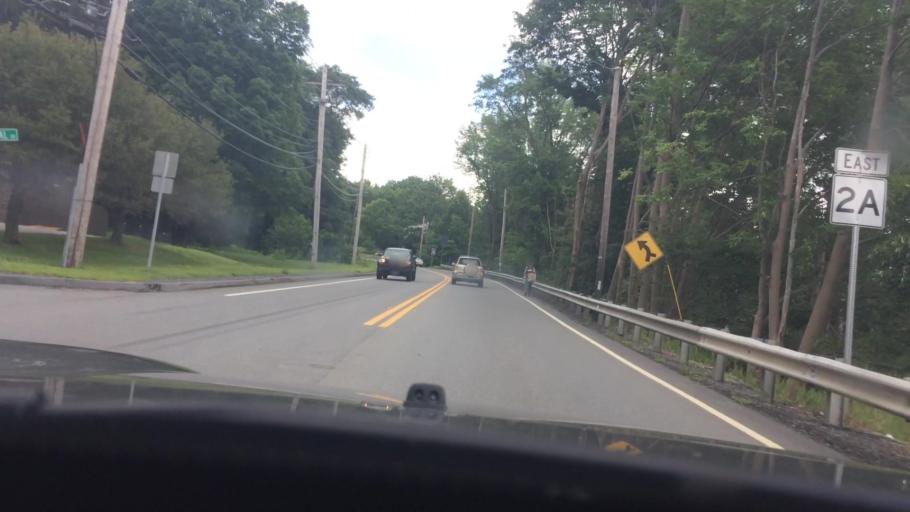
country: US
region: Massachusetts
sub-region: Worcester County
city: Athol
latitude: 42.5825
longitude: -72.2026
